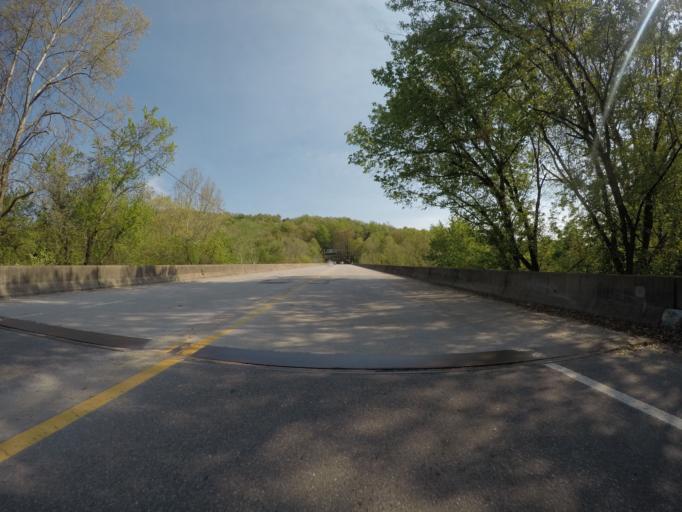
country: US
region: West Virginia
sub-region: Kanawha County
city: Pinch
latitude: 38.4056
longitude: -81.5417
